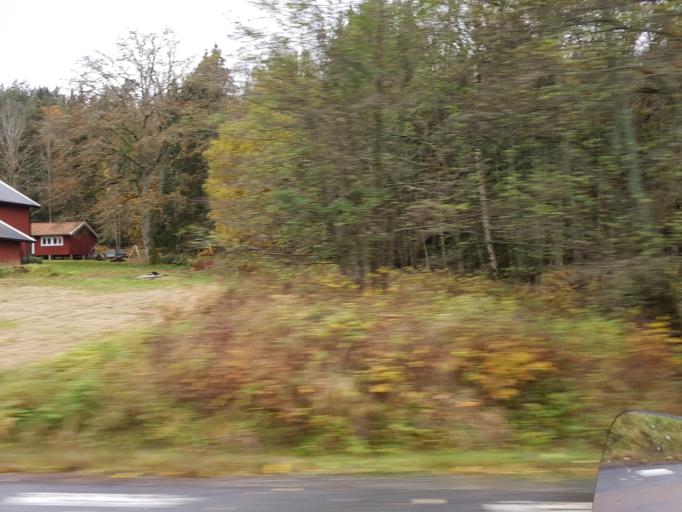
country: SE
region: Vaestra Goetaland
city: Svanesund
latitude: 58.2261
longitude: 11.8261
